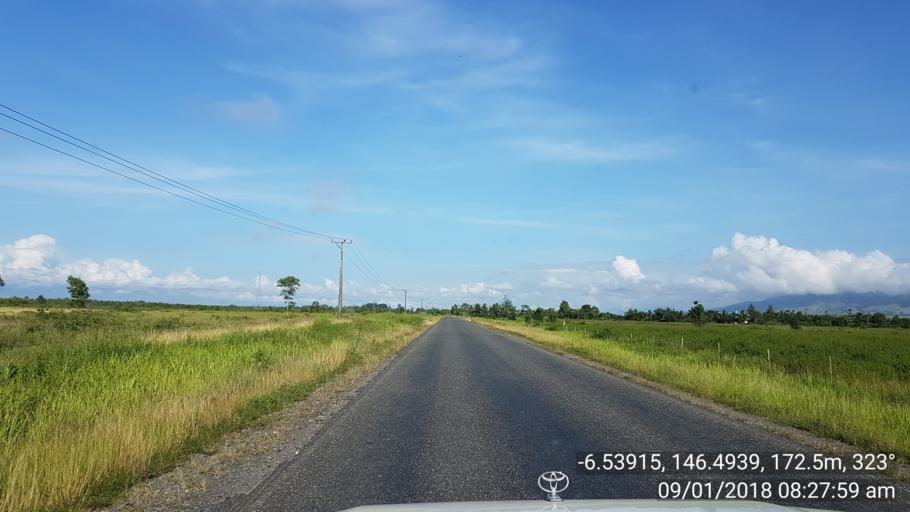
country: PG
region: Morobe
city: Lae
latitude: -6.5392
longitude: 146.4939
